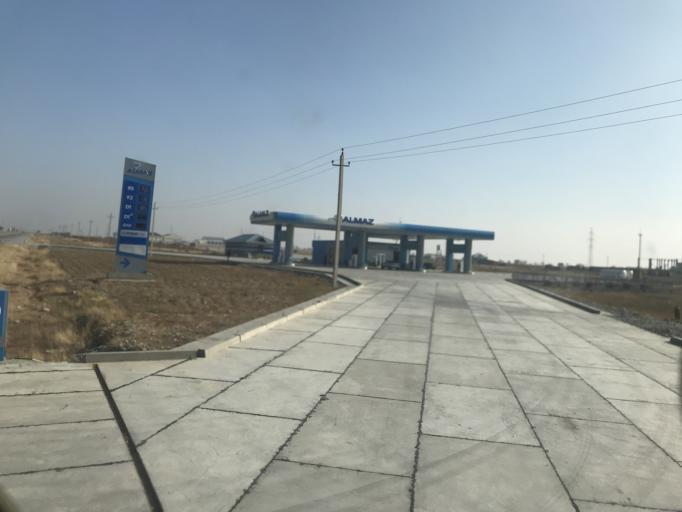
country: KZ
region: Ongtustik Qazaqstan
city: Shymkent
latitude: 42.4557
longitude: 69.6080
